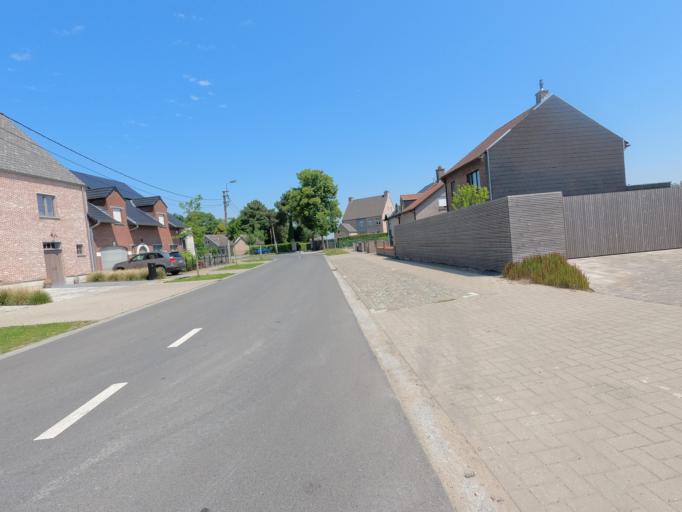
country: BE
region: Flanders
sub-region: Provincie Oost-Vlaanderen
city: Zele
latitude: 51.0452
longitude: 4.0276
